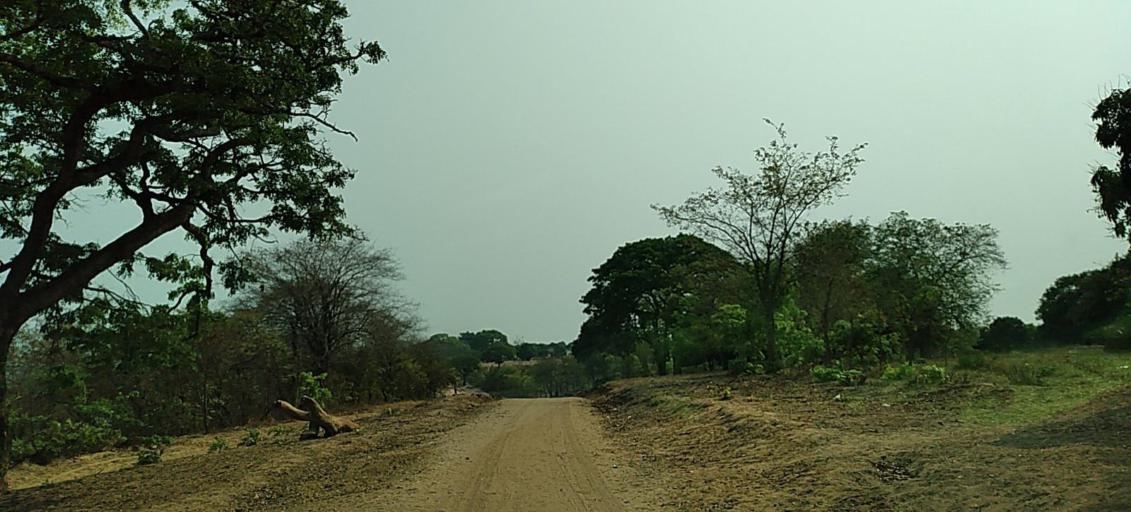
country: ZM
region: North-Western
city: Zambezi
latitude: -13.1794
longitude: 23.4008
